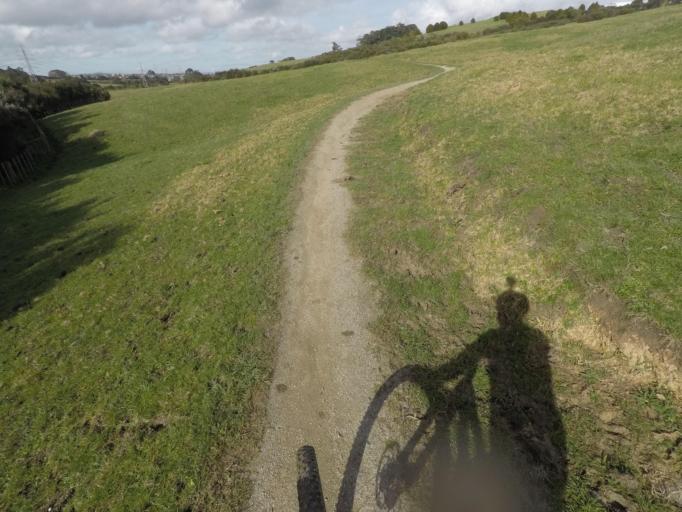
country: NZ
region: Auckland
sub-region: Auckland
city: Manukau City
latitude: -36.9918
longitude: 174.9070
